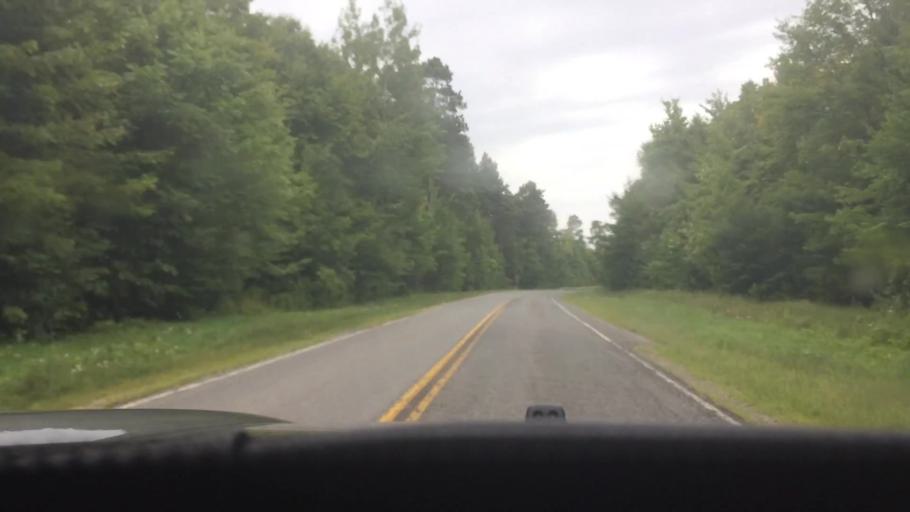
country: US
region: New York
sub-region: St. Lawrence County
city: Hannawa Falls
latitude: 44.6060
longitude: -74.8845
